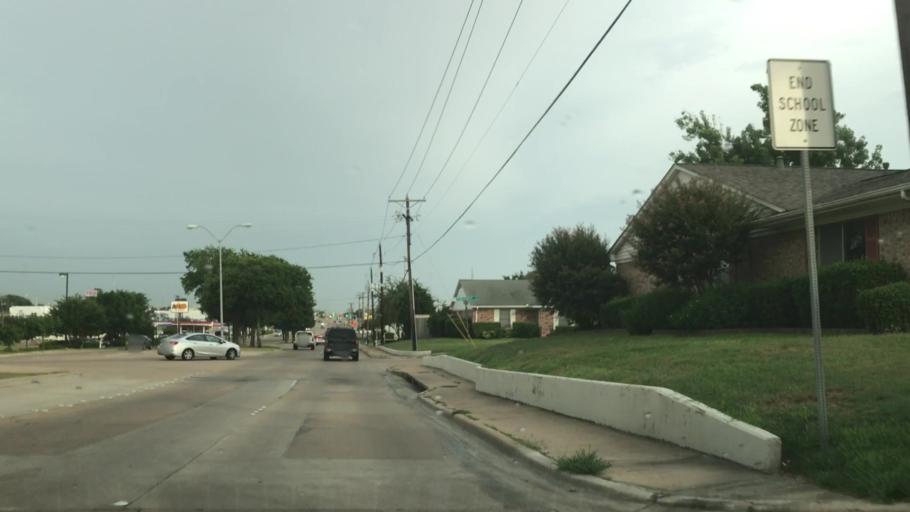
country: US
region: Texas
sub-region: Dallas County
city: Garland
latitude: 32.8355
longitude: -96.6361
